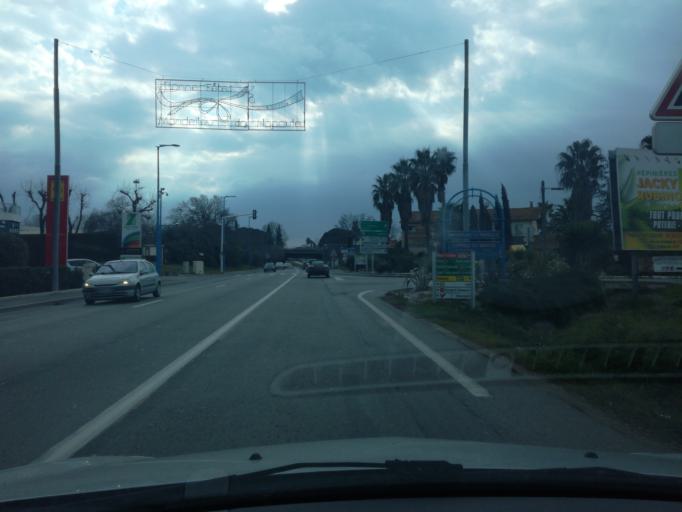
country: FR
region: Provence-Alpes-Cote d'Azur
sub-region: Departement des Alpes-Maritimes
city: Mandelieu-la-Napoule
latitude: 43.5598
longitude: 6.9511
